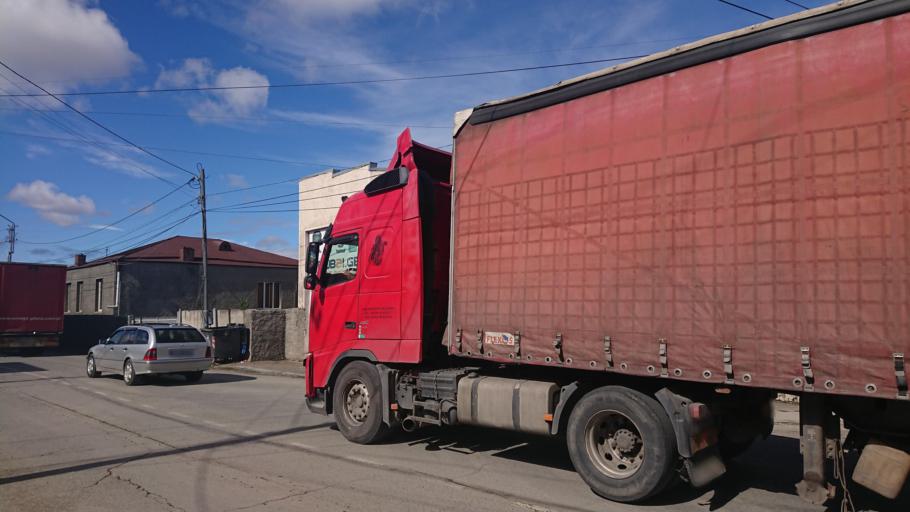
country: GE
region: Kakheti
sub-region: Telavi
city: Telavi
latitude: 41.9238
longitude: 45.4766
